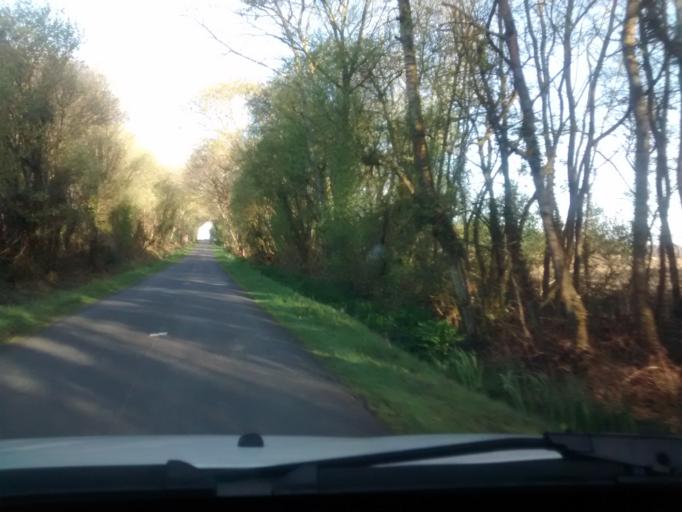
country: FR
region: Brittany
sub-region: Departement d'Ille-et-Vilaine
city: Saint-Broladre
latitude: 48.5563
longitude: -1.6304
